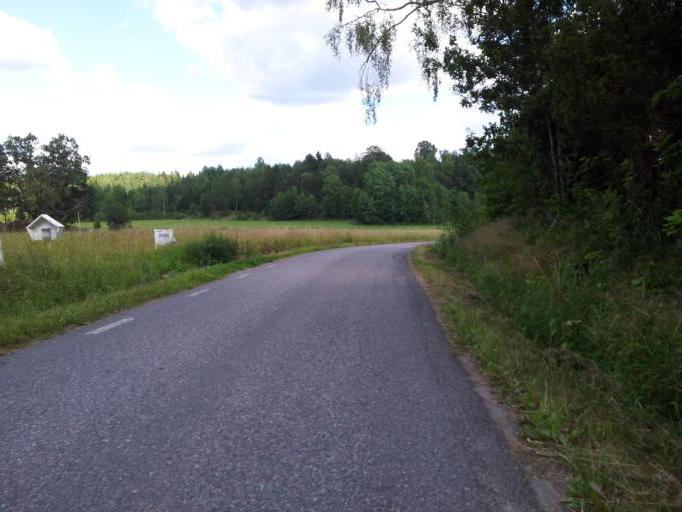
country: SE
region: Uppsala
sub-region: Knivsta Kommun
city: Knivsta
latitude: 59.8444
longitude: 17.9637
